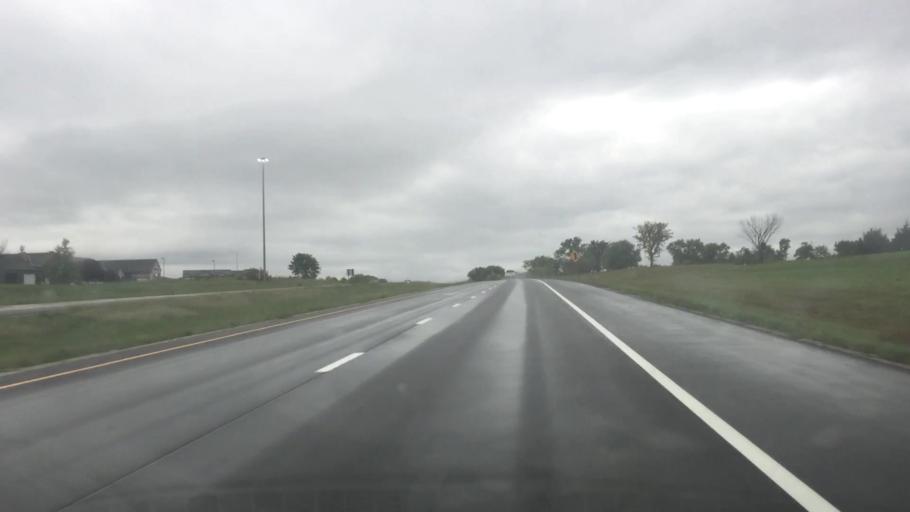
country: US
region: Kansas
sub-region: Johnson County
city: Spring Hill
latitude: 38.7234
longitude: -94.8345
